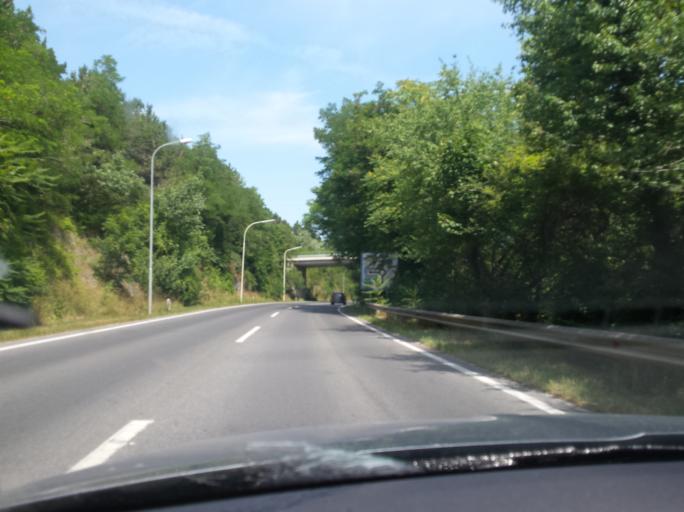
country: AT
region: Lower Austria
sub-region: Politischer Bezirk Bruck an der Leitha
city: Bad Deutsch-Altenburg
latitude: 48.1364
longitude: 16.9105
